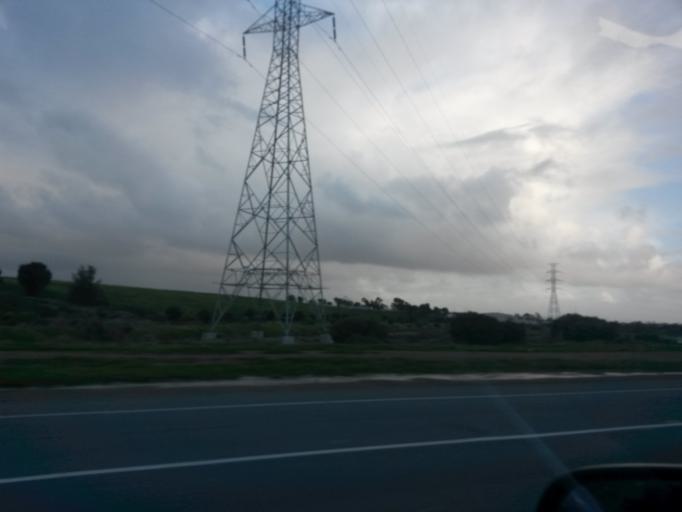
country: AU
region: South Australia
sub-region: Port Adelaide Enfield
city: Enfield
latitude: -34.8210
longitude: 138.5887
